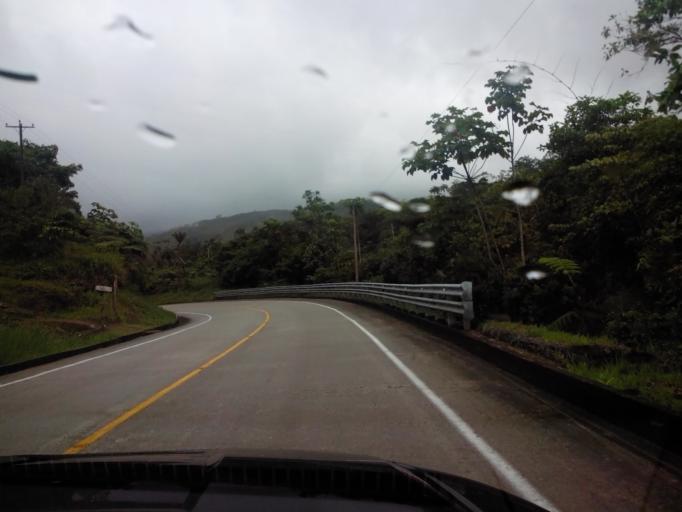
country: EC
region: Napo
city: Archidona
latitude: -0.7817
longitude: -77.7846
